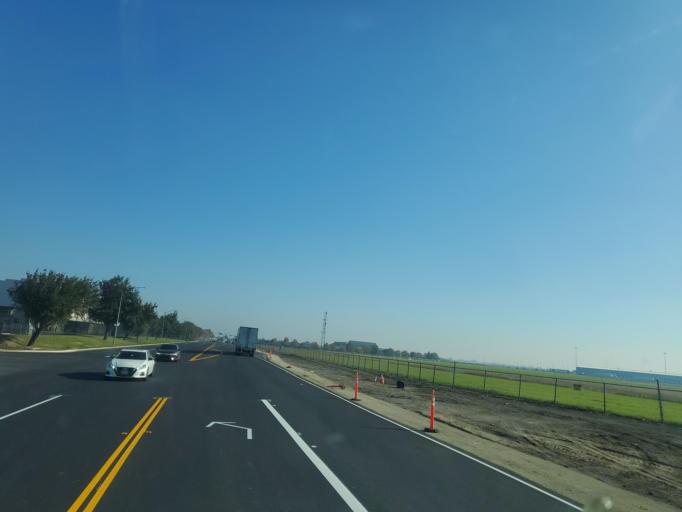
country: US
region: California
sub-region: San Joaquin County
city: Kennedy
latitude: 37.9043
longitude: -121.2490
